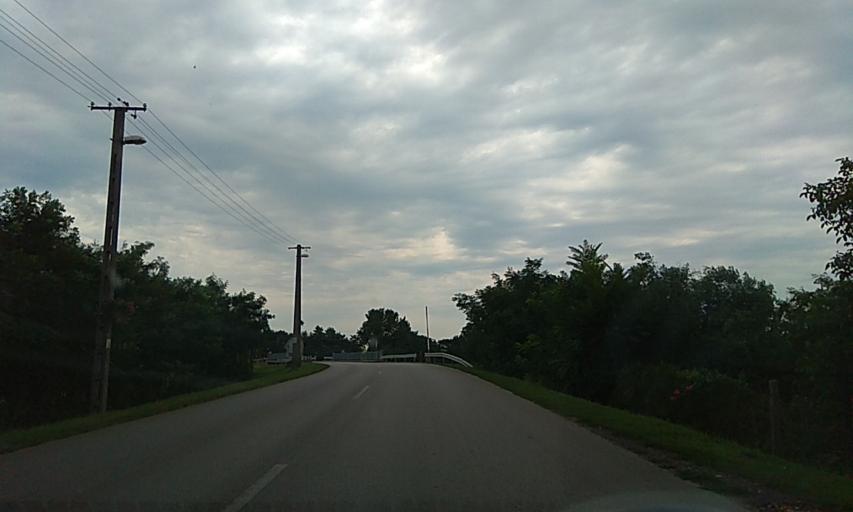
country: HU
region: Szabolcs-Szatmar-Bereg
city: Buj
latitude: 48.0934
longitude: 21.6403
